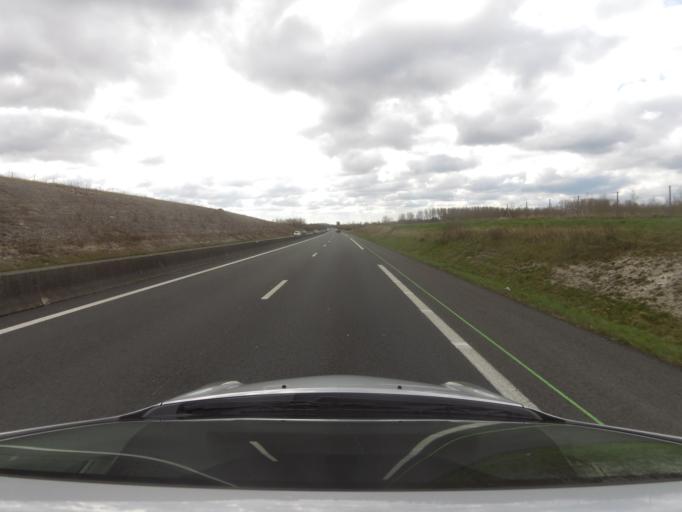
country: FR
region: Picardie
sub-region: Departement de la Somme
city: Quend
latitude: 50.3484
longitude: 1.6903
